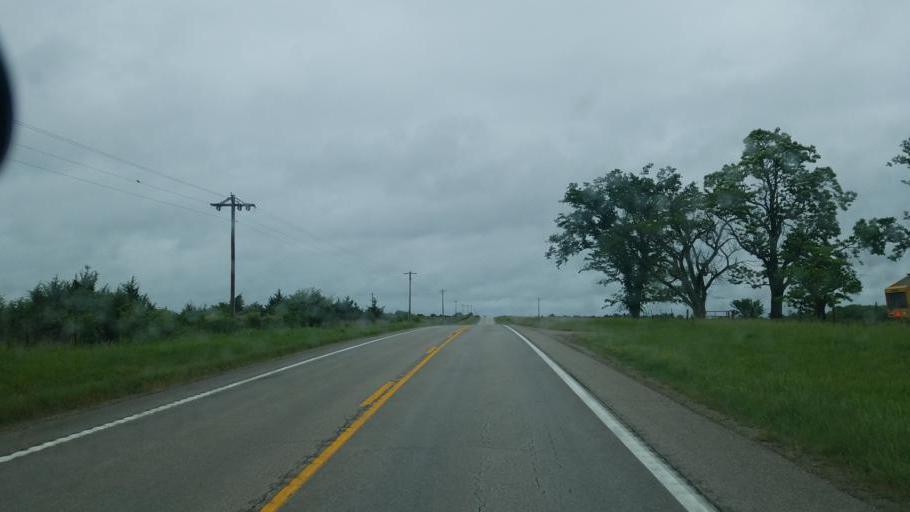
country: US
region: Missouri
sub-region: Carroll County
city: Carrollton
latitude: 39.5697
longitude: -93.4771
